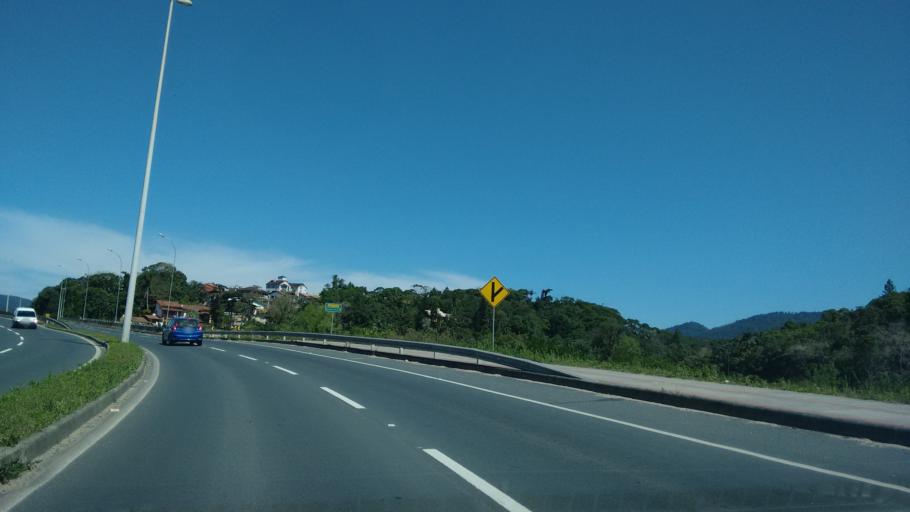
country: BR
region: Santa Catarina
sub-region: Blumenau
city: Blumenau
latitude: -26.8847
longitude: -49.1421
